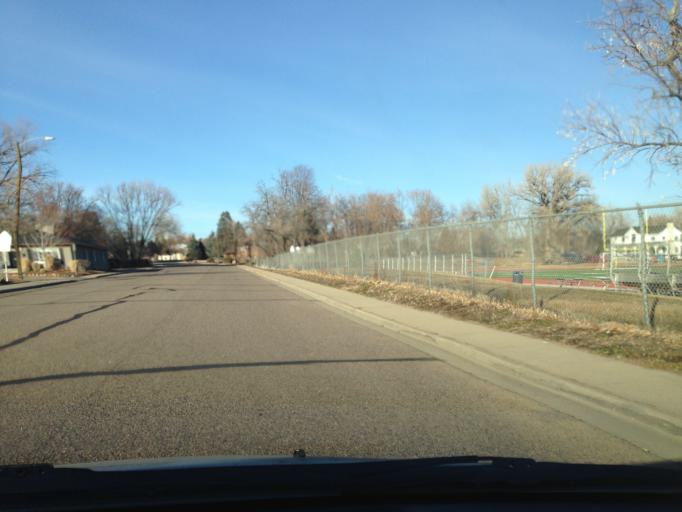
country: US
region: Colorado
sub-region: Boulder County
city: Louisville
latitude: 39.9840
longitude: -105.1345
